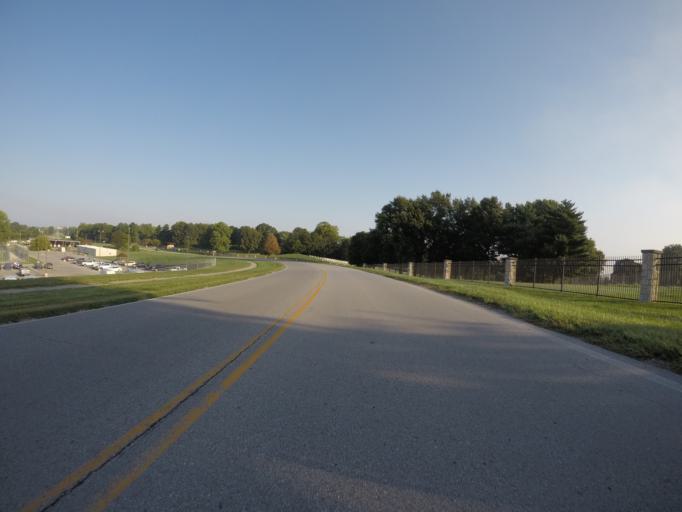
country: US
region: Kansas
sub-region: Leavenworth County
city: Lansing
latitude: 39.2733
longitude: -94.8907
